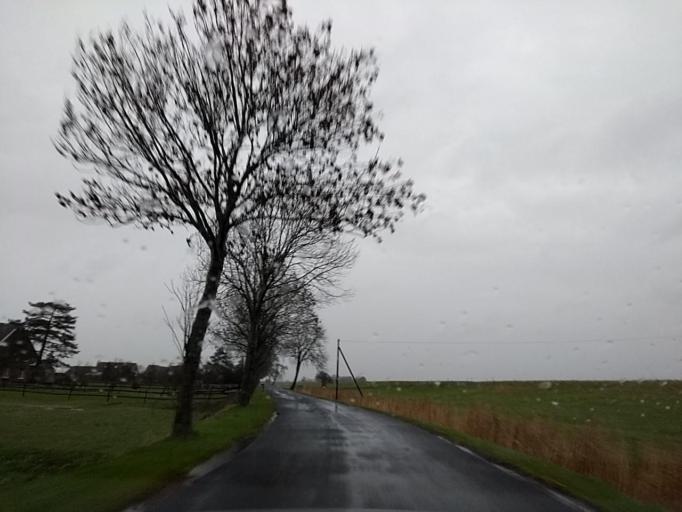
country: DE
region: Lower Saxony
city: Bunde
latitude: 53.2434
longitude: 7.2370
